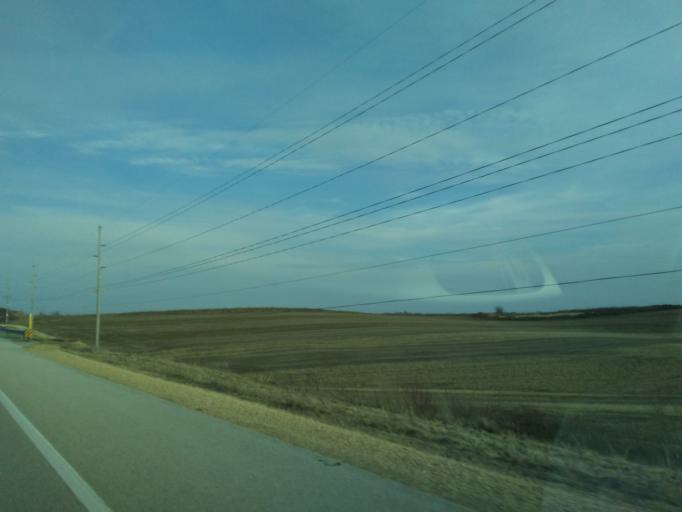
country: US
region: Wisconsin
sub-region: Iowa County
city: Dodgeville
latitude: 42.9746
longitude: -90.1830
